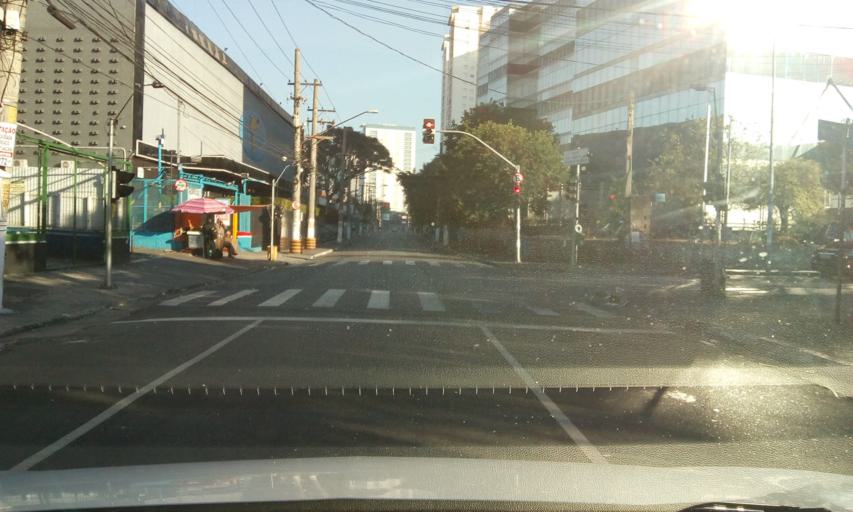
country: BR
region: Sao Paulo
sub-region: Sao Paulo
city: Sao Paulo
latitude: -23.5278
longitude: -46.6670
